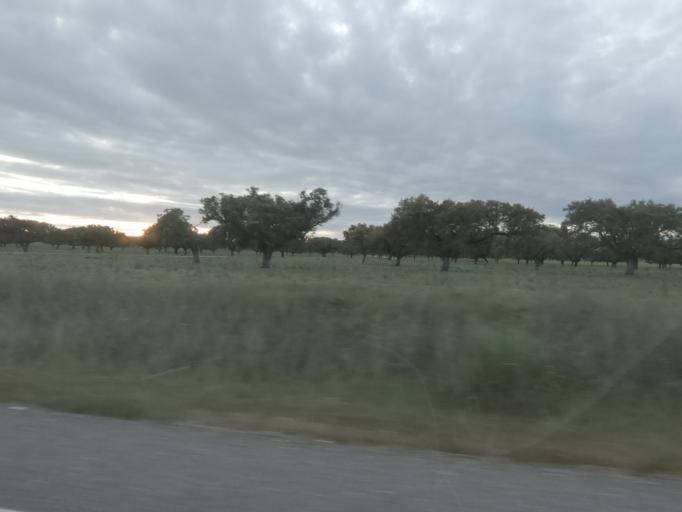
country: ES
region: Extremadura
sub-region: Provincia de Badajoz
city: La Roca de la Sierra
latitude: 39.0772
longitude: -6.7477
